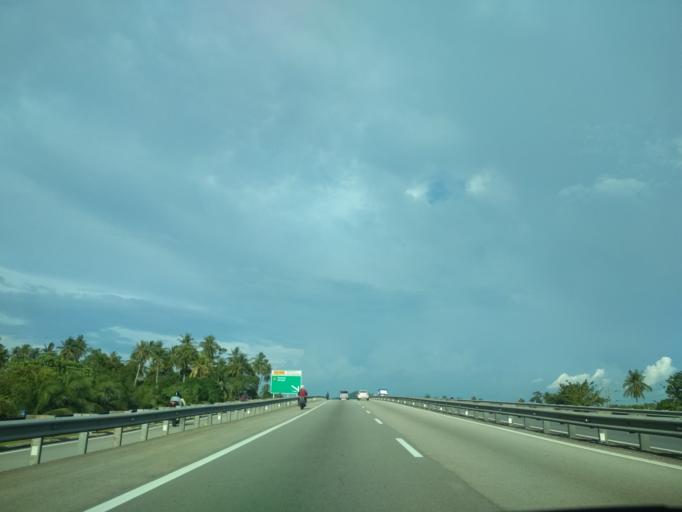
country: MY
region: Penang
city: Bukit Mertajam
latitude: 5.4025
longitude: 100.4697
